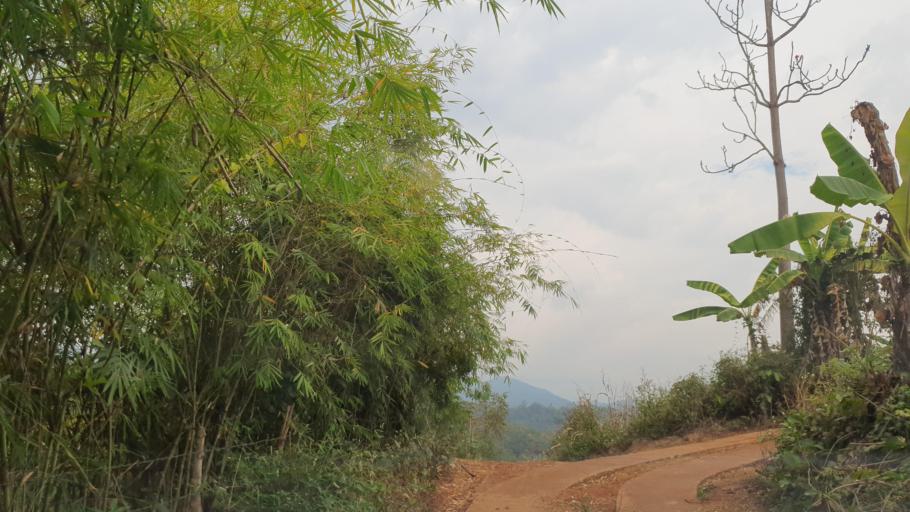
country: TH
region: Chiang Mai
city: Mae Wang
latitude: 18.6563
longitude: 98.6510
